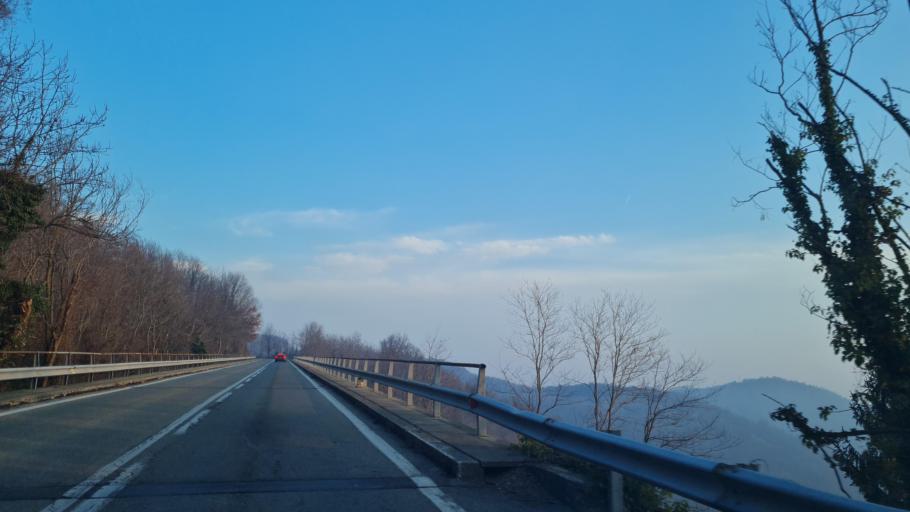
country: IT
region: Piedmont
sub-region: Provincia di Torino
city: Andrate
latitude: 45.5212
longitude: 7.8717
